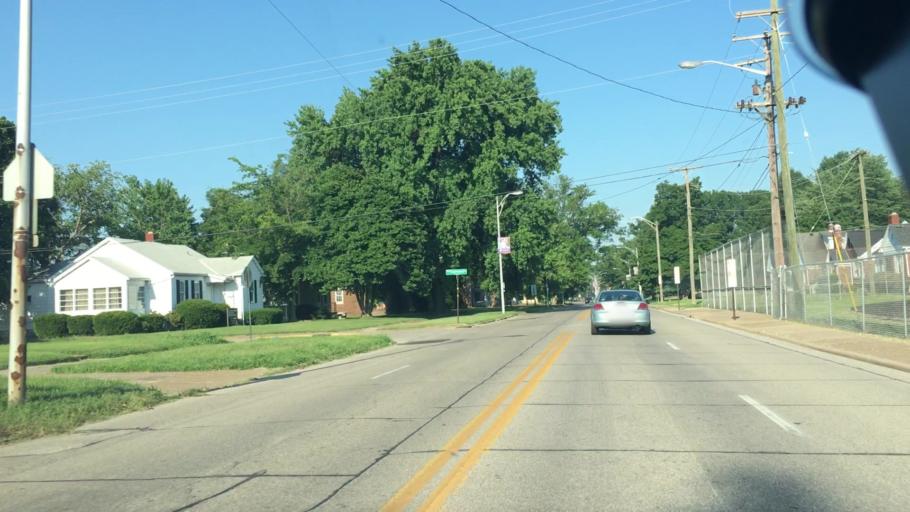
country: US
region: Indiana
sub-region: Vanderburgh County
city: Evansville
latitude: 37.9735
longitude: -87.5366
